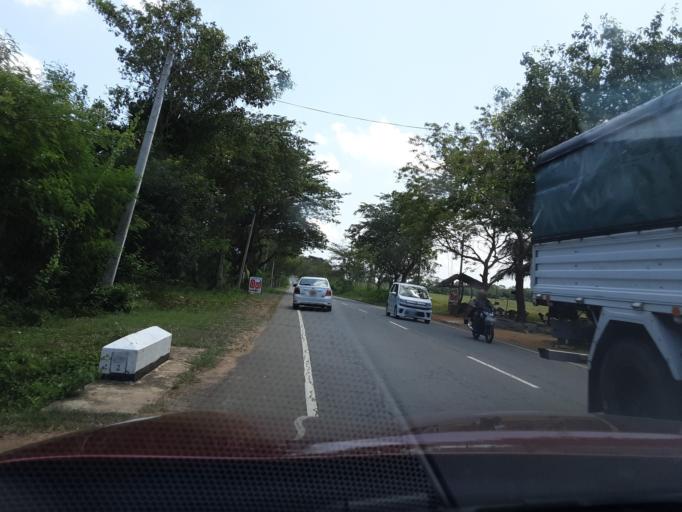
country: LK
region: Southern
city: Tangalla
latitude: 6.2317
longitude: 81.2259
